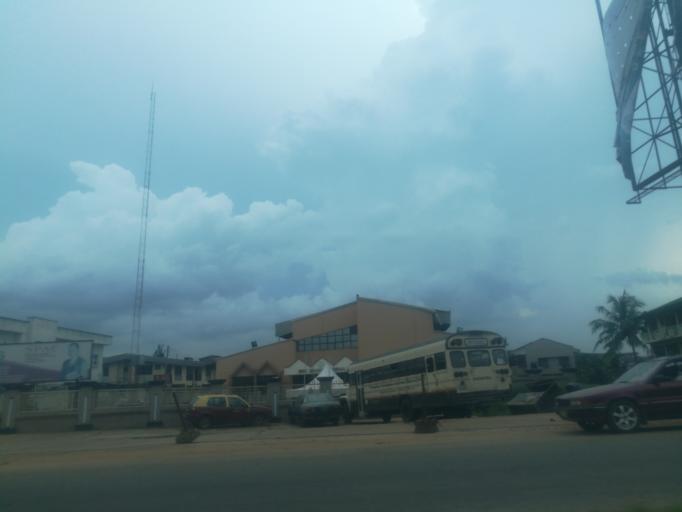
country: NG
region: Oyo
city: Ibadan
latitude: 7.4268
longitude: 3.8952
